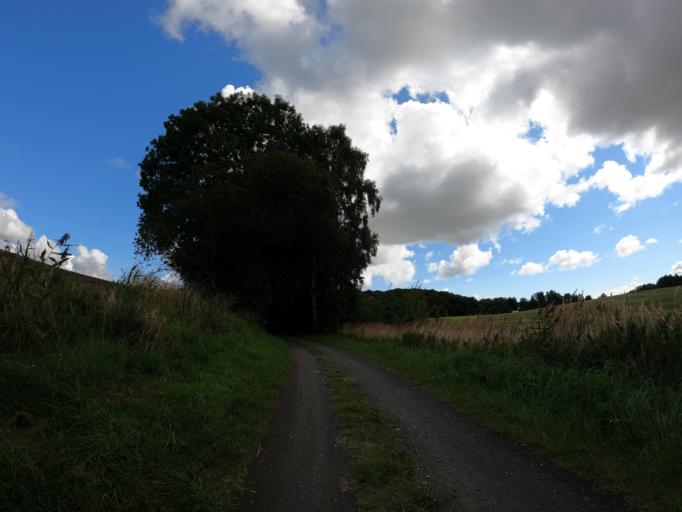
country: DE
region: Mecklenburg-Vorpommern
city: Sehlen
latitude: 54.3546
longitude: 13.4026
